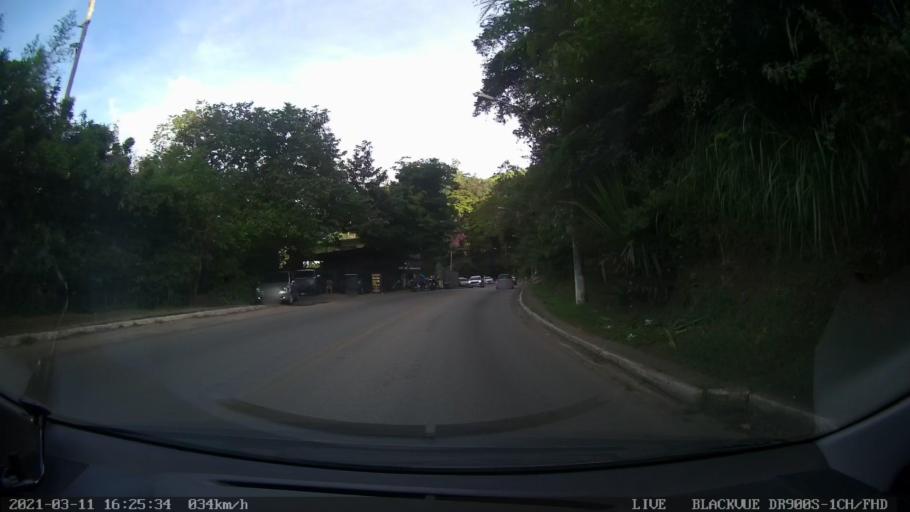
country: BR
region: Rio de Janeiro
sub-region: Petropolis
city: Petropolis
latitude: -22.4165
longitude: -43.1389
